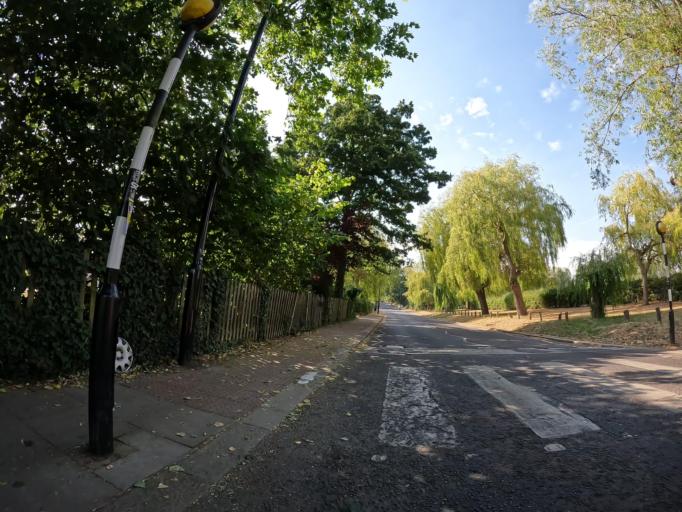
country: GB
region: England
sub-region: Hertfordshire
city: Potters Bar
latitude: 51.6882
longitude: -0.1583
